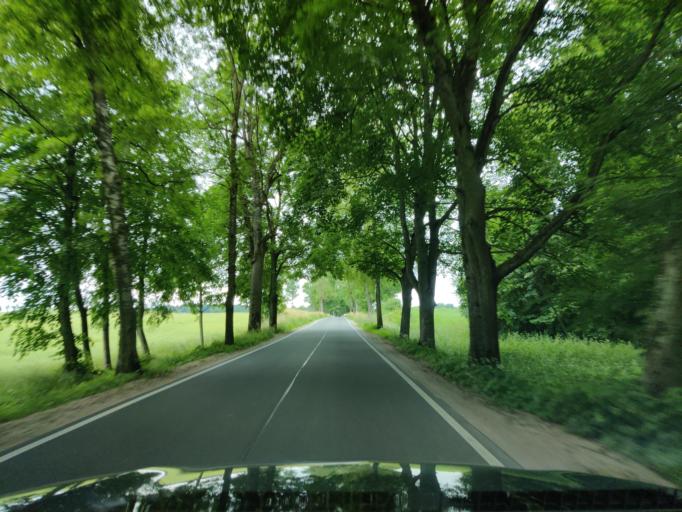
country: PL
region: Warmian-Masurian Voivodeship
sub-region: Powiat gizycki
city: Ryn
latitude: 53.9094
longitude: 21.5611
